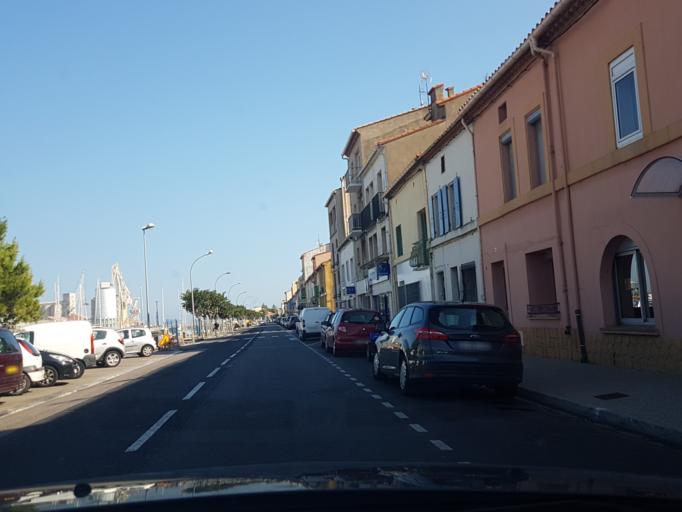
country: FR
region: Languedoc-Roussillon
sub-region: Departement de l'Aude
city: Port-la-Nouvelle
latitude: 43.0228
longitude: 3.0441
